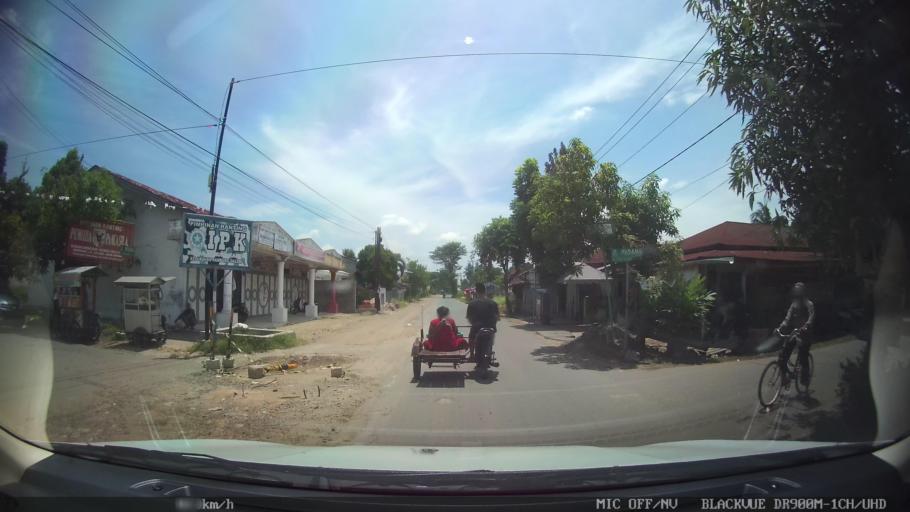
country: ID
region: North Sumatra
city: Binjai
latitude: 3.5940
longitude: 98.4931
